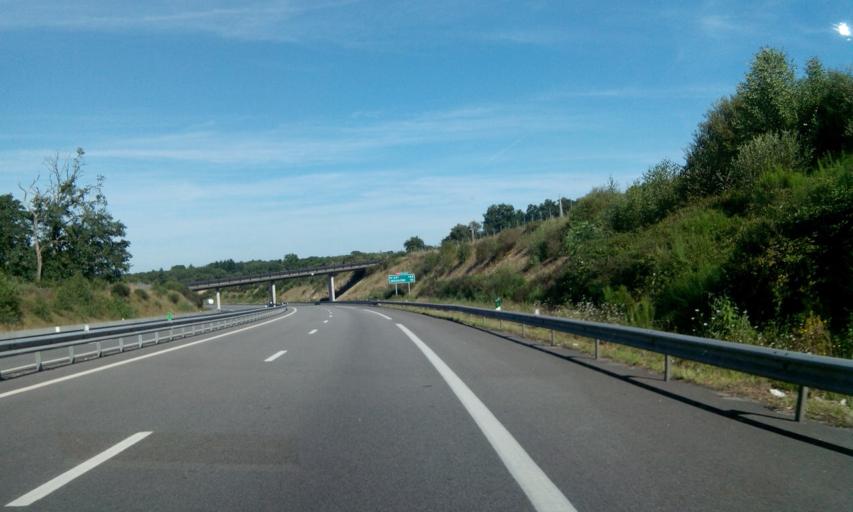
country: FR
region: Limousin
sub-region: Departement de la Haute-Vienne
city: Verneuil-sur-Vienne
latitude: 45.8633
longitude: 1.1369
